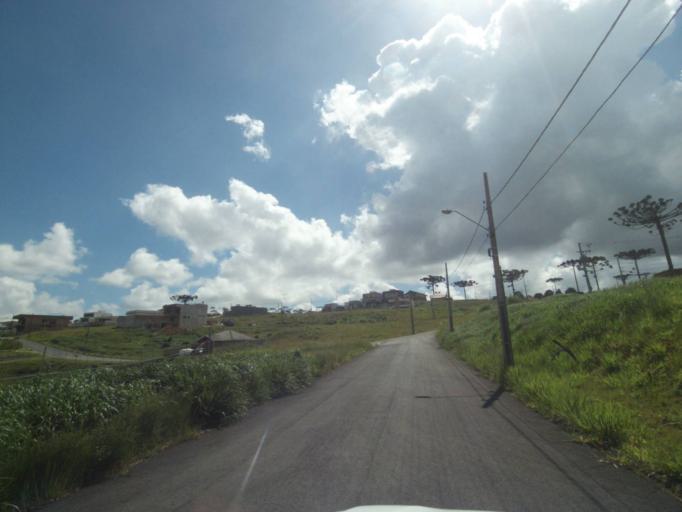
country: BR
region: Parana
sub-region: Colombo
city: Colombo
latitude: -25.3132
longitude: -49.2349
